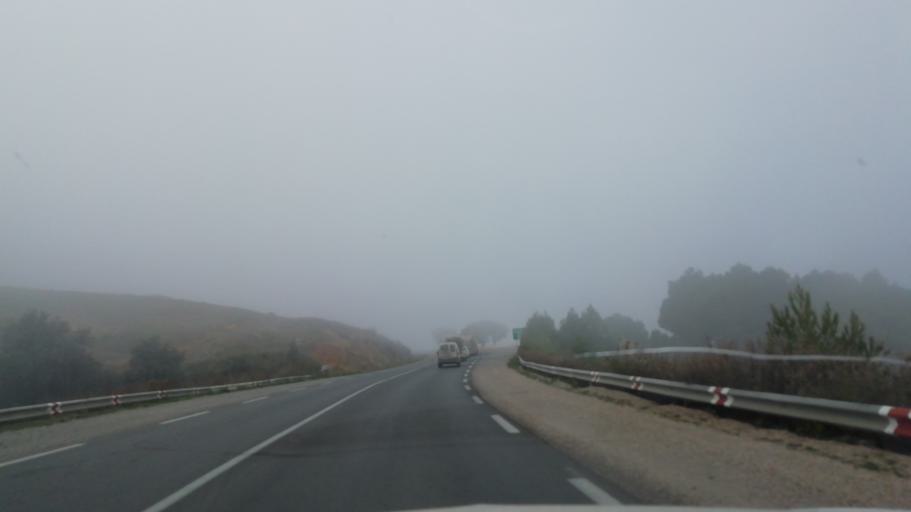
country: DZ
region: Mascara
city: Mascara
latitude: 35.5272
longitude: 0.3284
